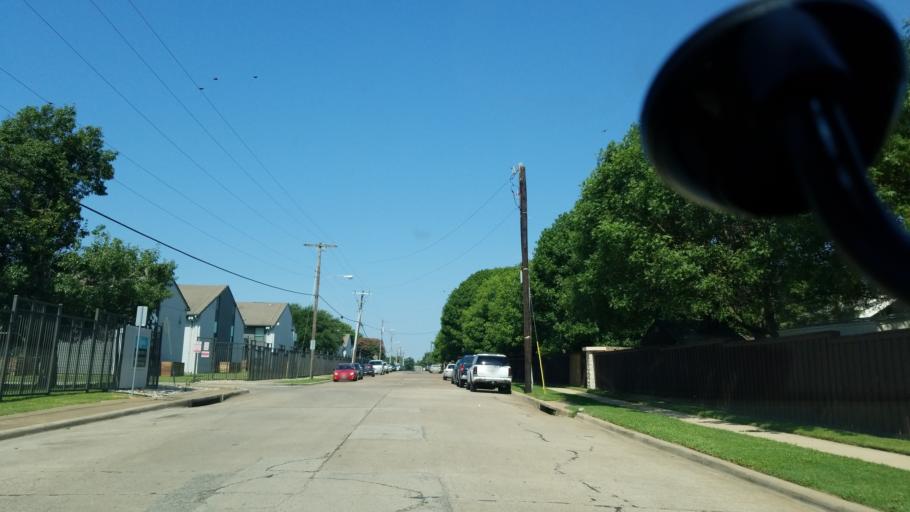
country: US
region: Texas
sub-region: Dallas County
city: Cockrell Hill
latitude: 32.7084
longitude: -96.8688
